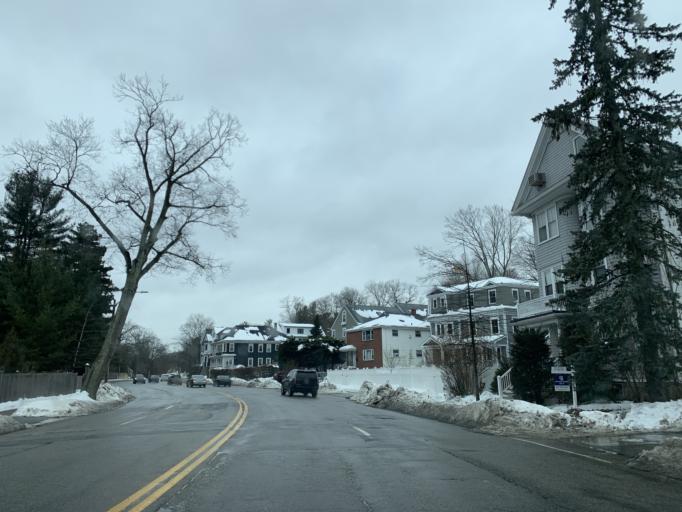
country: US
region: Massachusetts
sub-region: Norfolk County
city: Brookline
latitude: 42.3215
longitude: -71.1632
